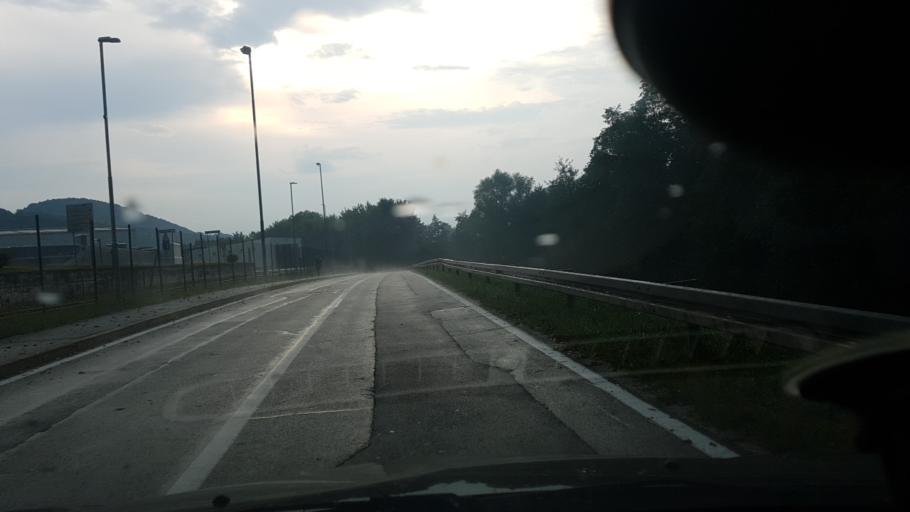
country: SI
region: Rogatec
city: Rogatec
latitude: 46.2230
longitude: 15.7110
